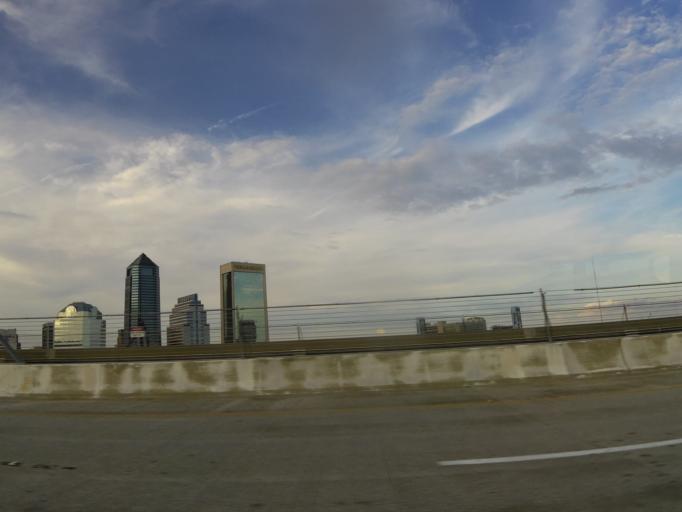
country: US
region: Florida
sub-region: Duval County
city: Jacksonville
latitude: 30.3209
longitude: -81.6648
